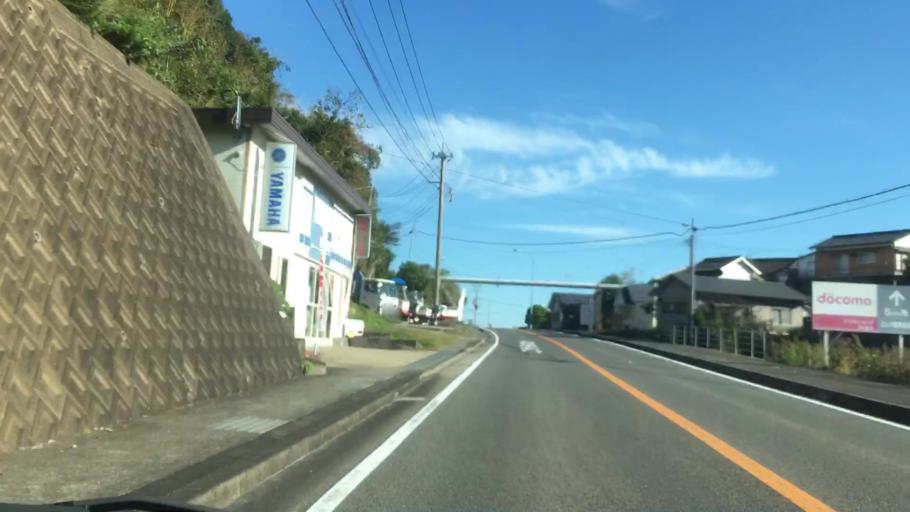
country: JP
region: Nagasaki
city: Sasebo
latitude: 33.0034
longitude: 129.7304
